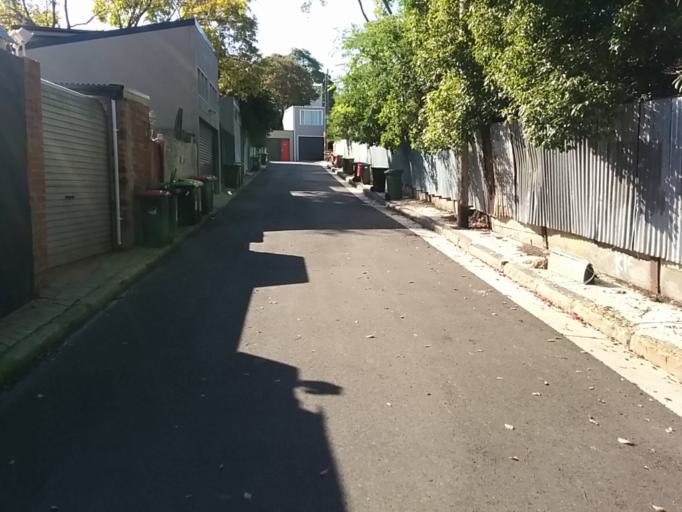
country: AU
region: New South Wales
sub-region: City of Sydney
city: Darlington
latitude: -33.8955
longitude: 151.1881
